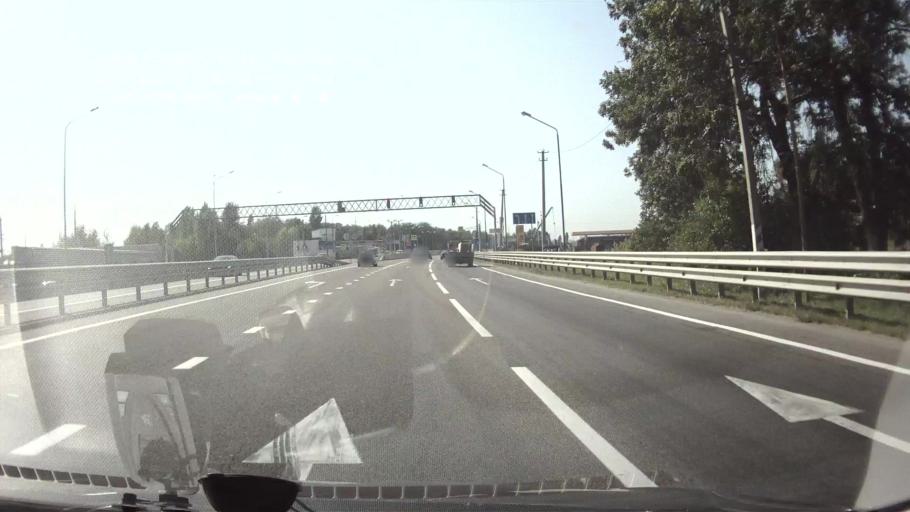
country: RU
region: Krasnodarskiy
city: Pashkovskiy
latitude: 45.0211
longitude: 39.2021
